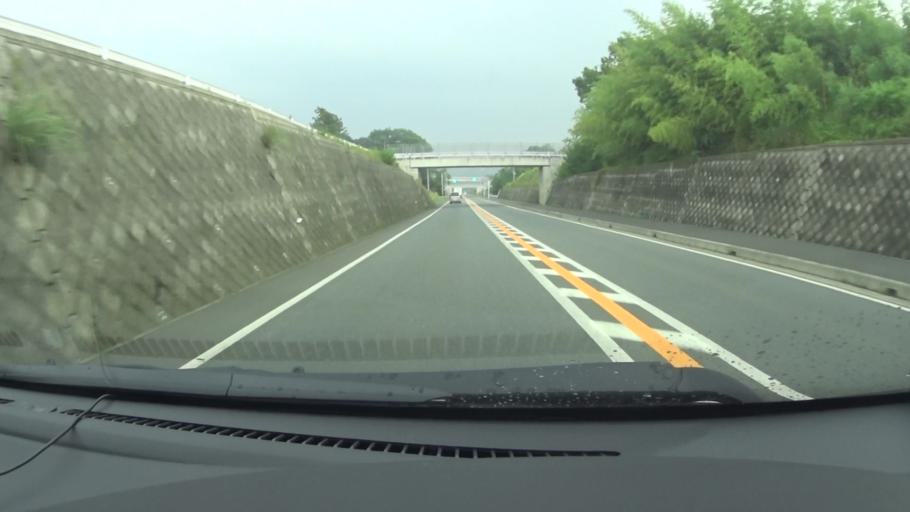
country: JP
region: Kyoto
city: Ayabe
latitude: 35.2044
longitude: 135.4325
